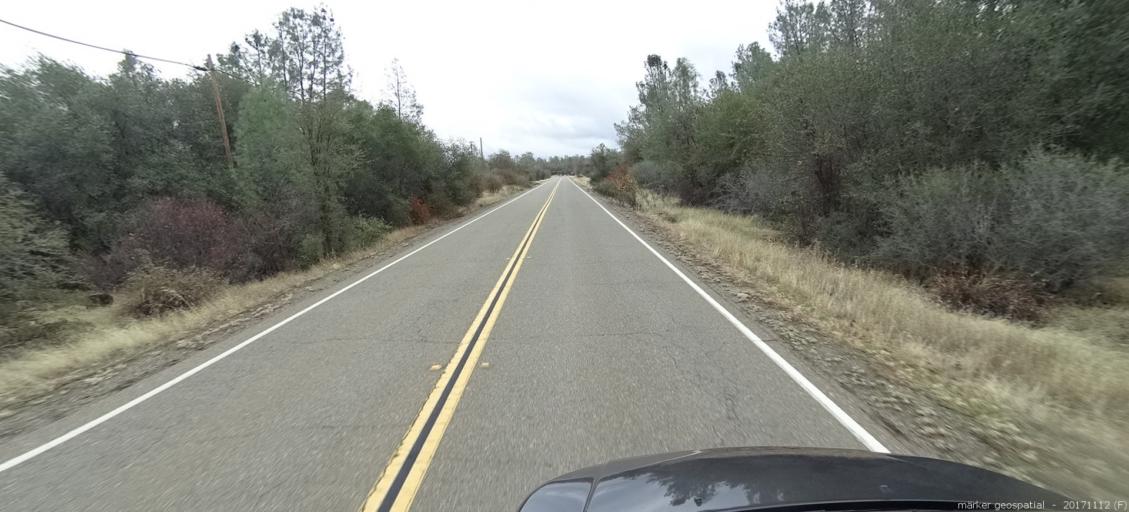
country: US
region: California
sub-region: Shasta County
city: Palo Cedro
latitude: 40.4811
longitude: -122.0885
